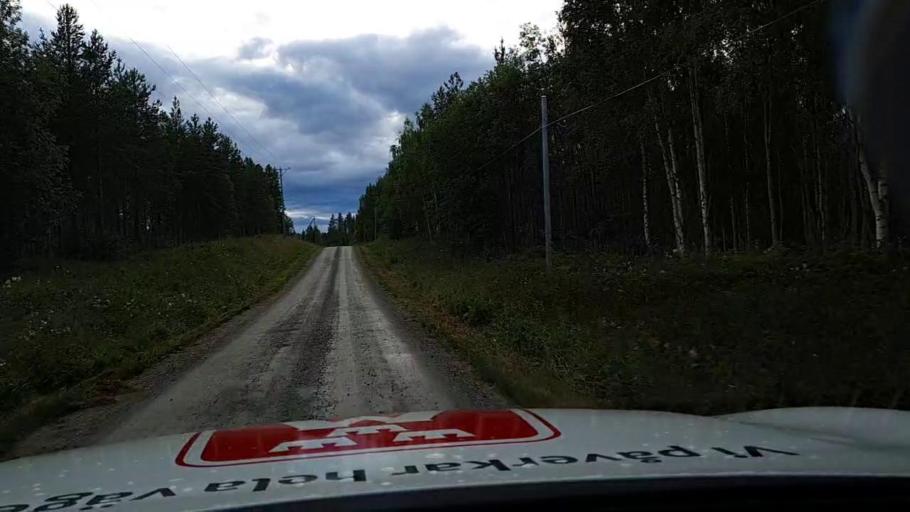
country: SE
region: Jaemtland
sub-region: Bergs Kommun
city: Hoverberg
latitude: 62.8919
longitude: 14.5607
